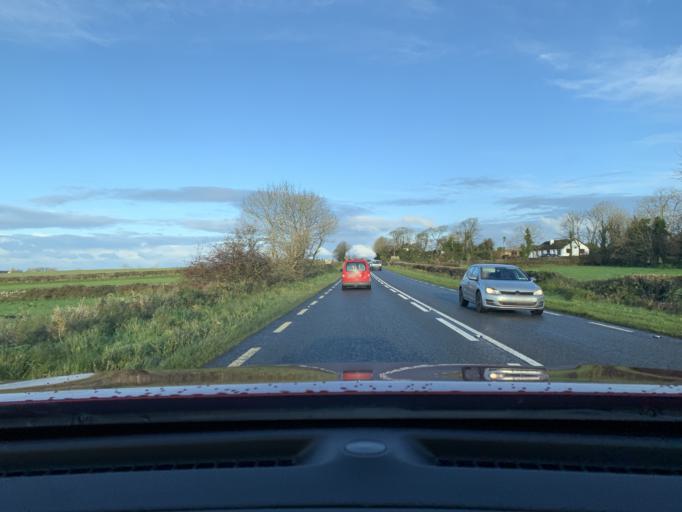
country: IE
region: Connaught
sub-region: Sligo
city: Sligo
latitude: 54.3551
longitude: -8.5151
